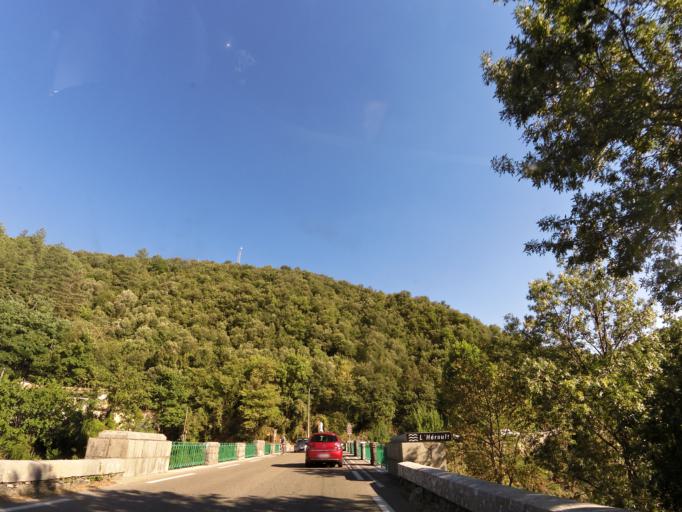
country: FR
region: Languedoc-Roussillon
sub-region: Departement du Gard
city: Sumene
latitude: 43.9963
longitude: 3.6775
